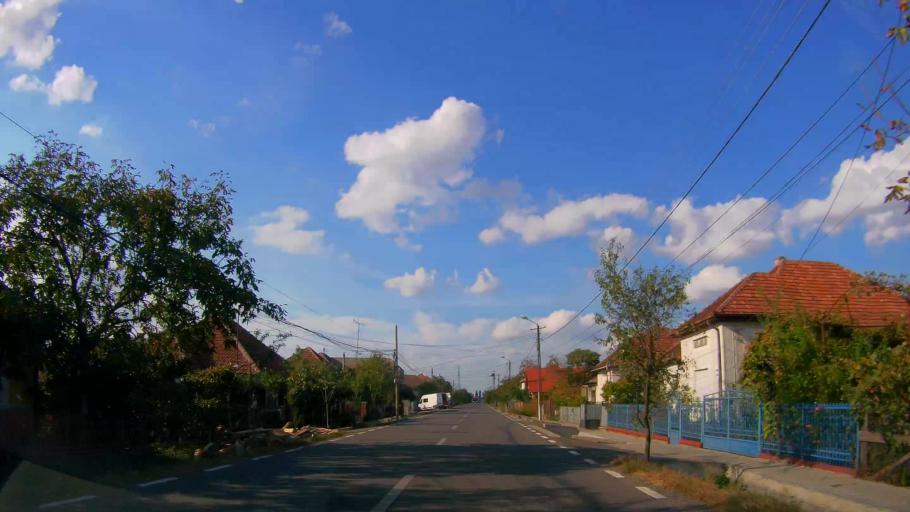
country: RO
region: Satu Mare
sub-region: Comuna Halmeu
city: Halmeu
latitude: 47.9864
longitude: 23.0063
